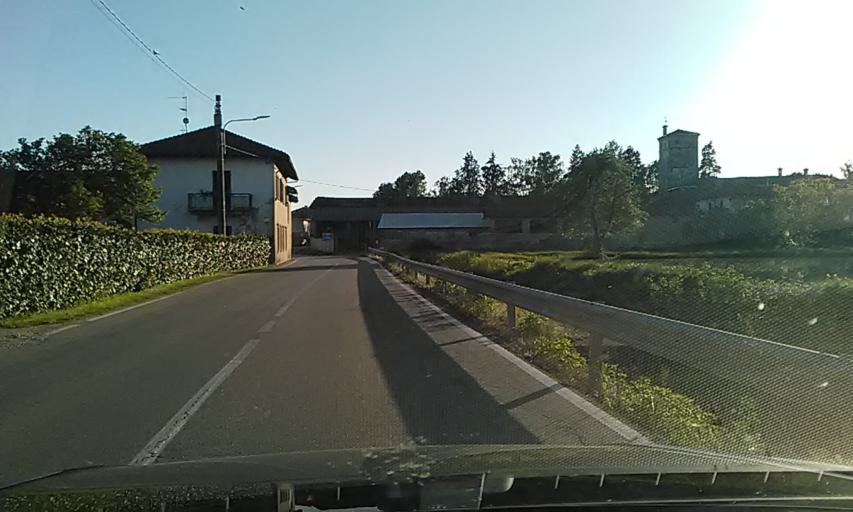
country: IT
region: Piedmont
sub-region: Provincia di Novara
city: Momo
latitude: 45.5693
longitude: 8.5432
